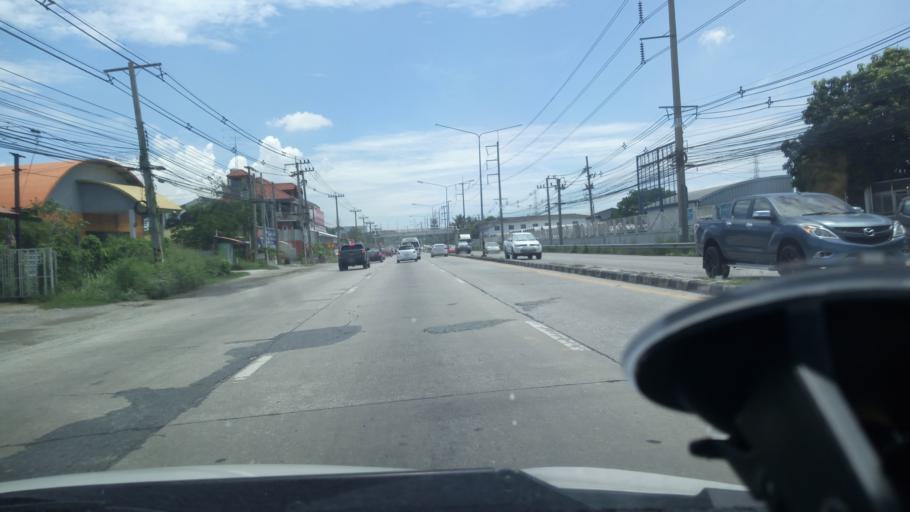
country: TH
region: Chon Buri
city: Chon Buri
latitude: 13.4021
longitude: 101.0328
